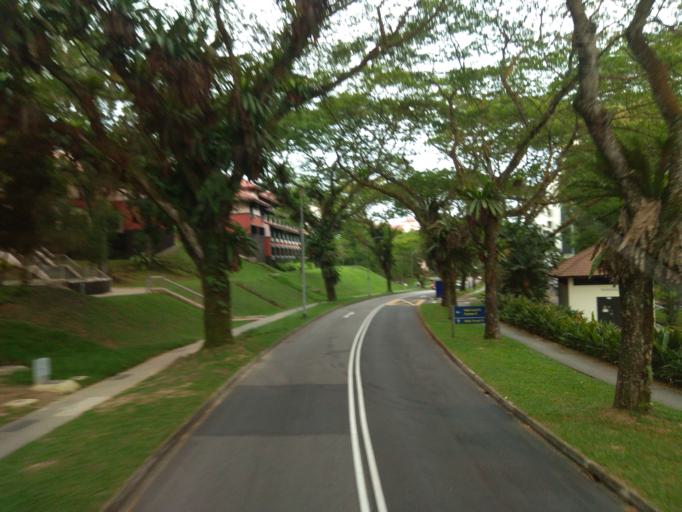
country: MY
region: Johor
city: Johor Bahru
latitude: 1.3519
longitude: 103.6858
